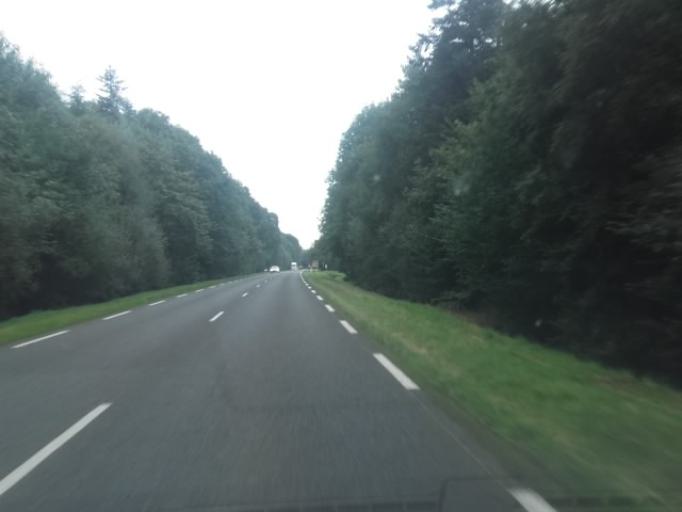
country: FR
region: Brittany
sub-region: Departement des Cotes-d'Armor
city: Plelo
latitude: 48.5850
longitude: -2.9365
